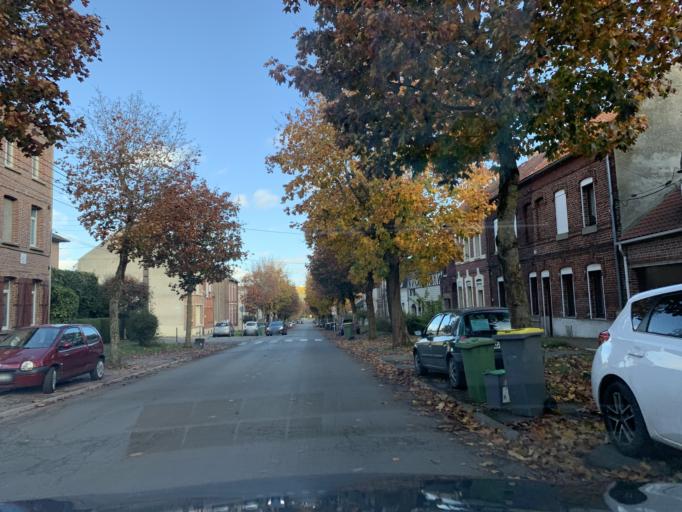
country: FR
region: Nord-Pas-de-Calais
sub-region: Departement du Nord
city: Cambrai
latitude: 50.1829
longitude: 3.2467
